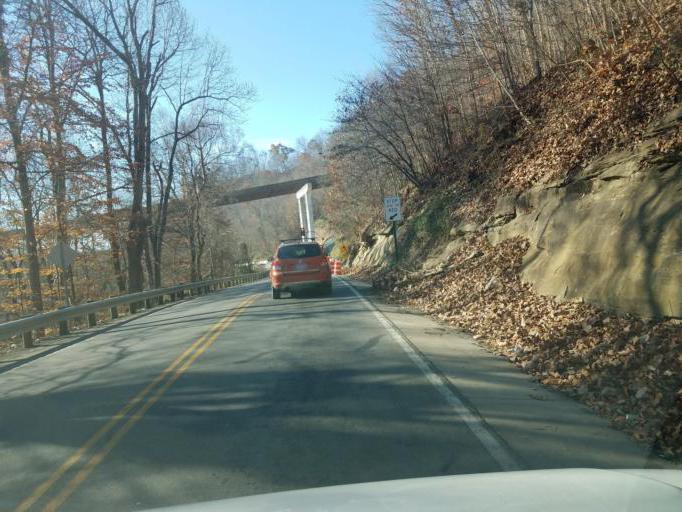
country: US
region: Ohio
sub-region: Scioto County
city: Sciotodale
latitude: 38.7750
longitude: -82.8711
